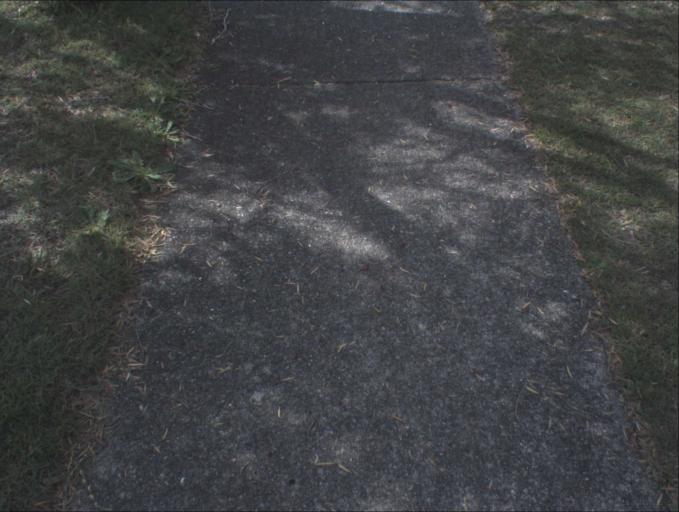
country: AU
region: Queensland
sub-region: Logan
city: Woodridge
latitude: -27.6617
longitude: 153.0596
